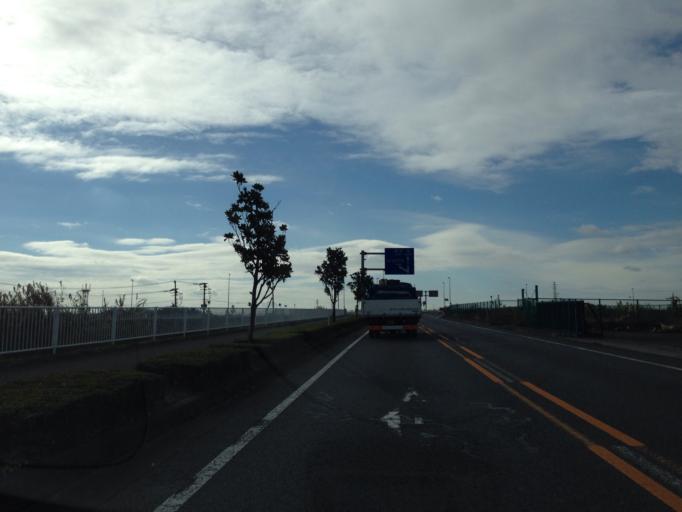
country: JP
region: Ibaraki
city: Fujishiro
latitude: 35.9288
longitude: 140.1159
